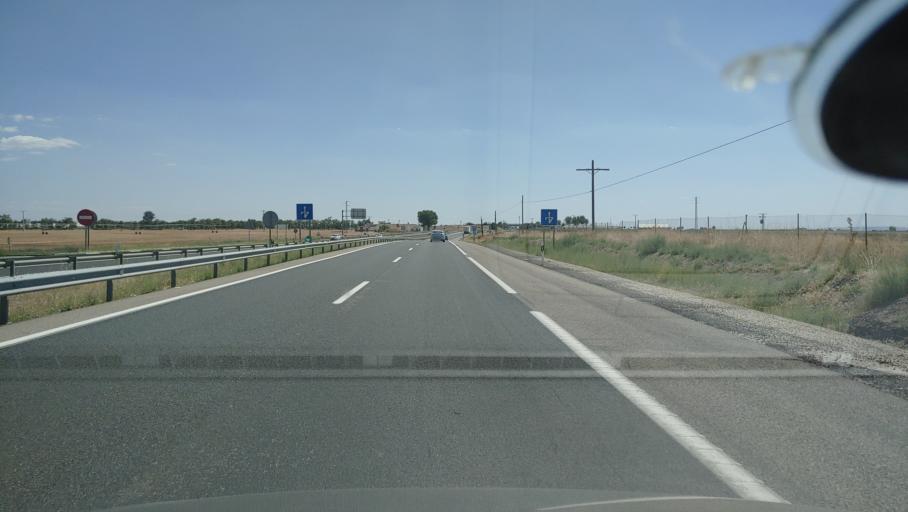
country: ES
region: Castille-La Mancha
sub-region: Provincia de Ciudad Real
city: Villarta de San Juan
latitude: 39.1303
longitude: -3.3794
